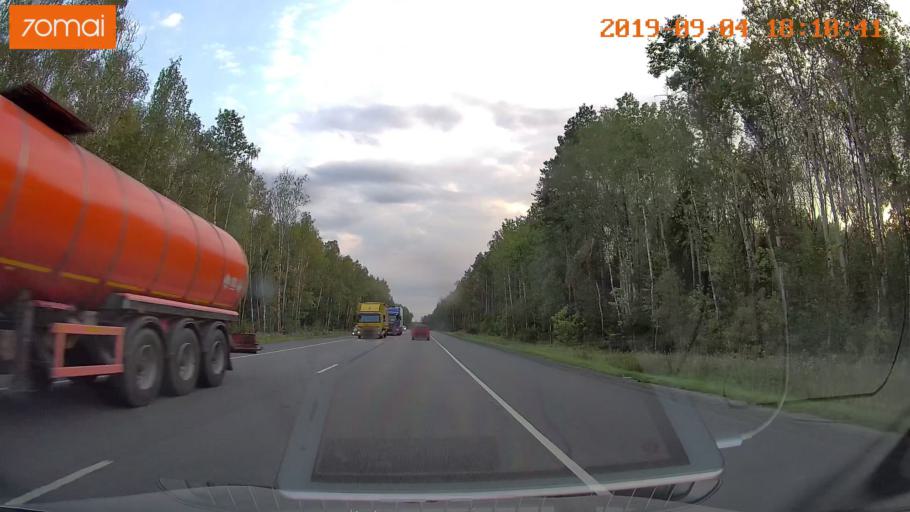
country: RU
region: Moskovskaya
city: Lopatinskiy
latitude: 55.3854
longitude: 38.7627
